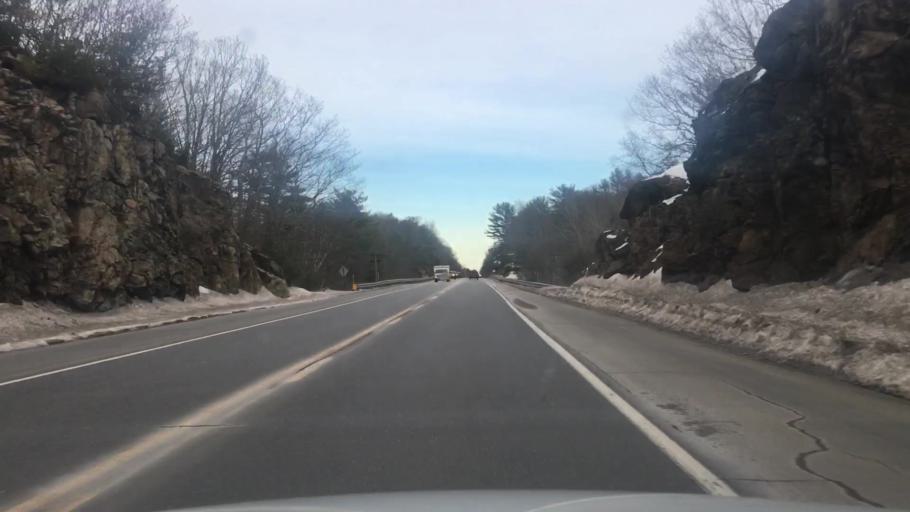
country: US
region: Maine
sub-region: Sagadahoc County
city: Woolwich
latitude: 43.9357
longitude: -69.7776
